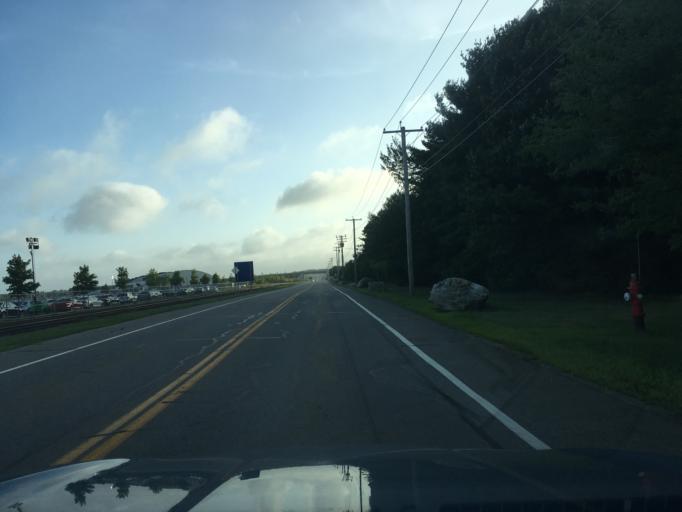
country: US
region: Rhode Island
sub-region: Kent County
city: East Greenwich
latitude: 41.6105
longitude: -71.4323
